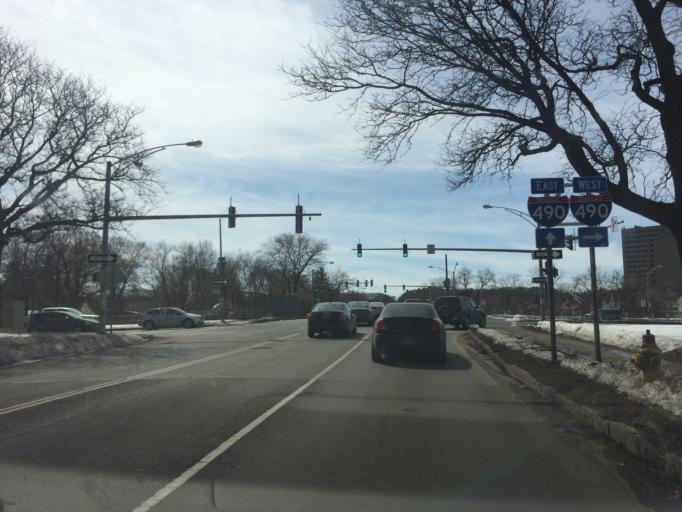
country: US
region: New York
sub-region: Monroe County
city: Rochester
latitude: 43.1425
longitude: -77.5944
